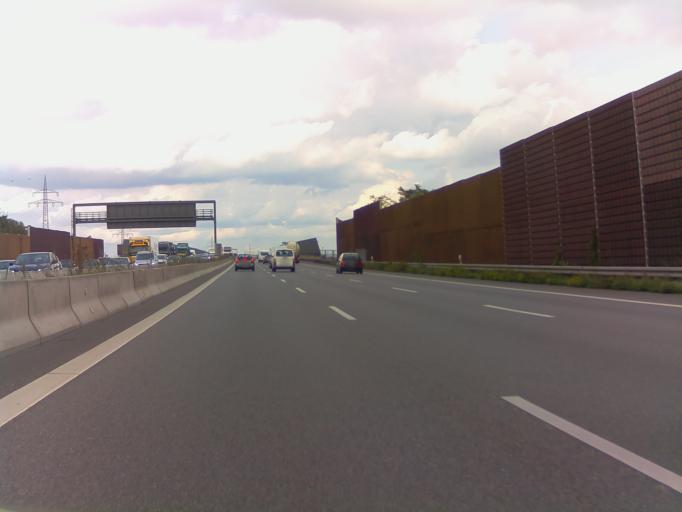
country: DE
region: Baden-Wuerttemberg
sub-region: Karlsruhe Region
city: Ilvesheim
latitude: 49.4718
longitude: 8.5419
